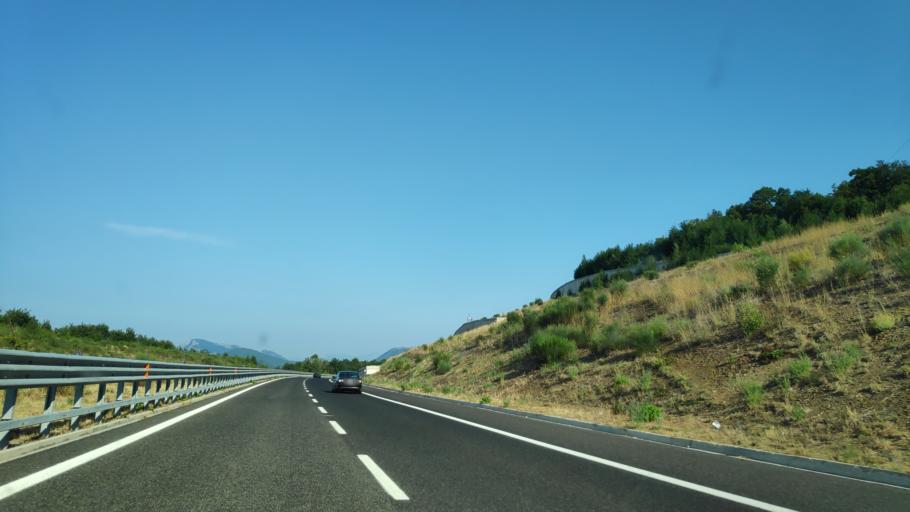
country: IT
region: Basilicate
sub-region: Provincia di Potenza
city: Nemoli
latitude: 40.1013
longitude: 15.8010
